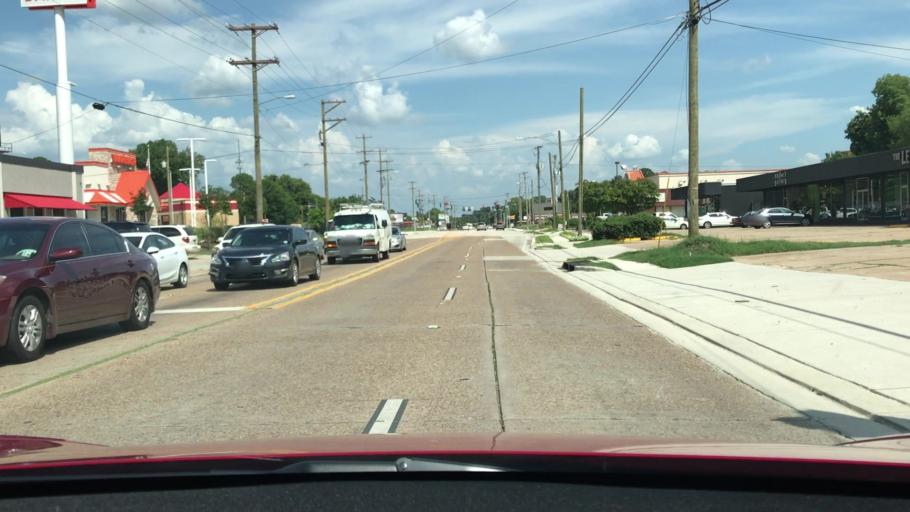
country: US
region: Louisiana
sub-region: Bossier Parish
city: Bossier City
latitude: 32.4809
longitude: -93.7246
